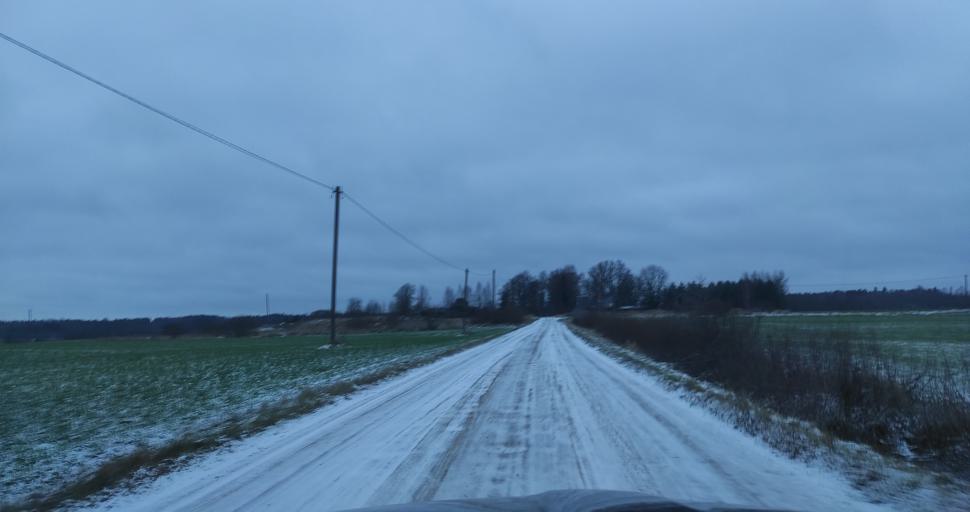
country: LV
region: Kuldigas Rajons
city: Kuldiga
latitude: 56.9705
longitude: 22.0611
